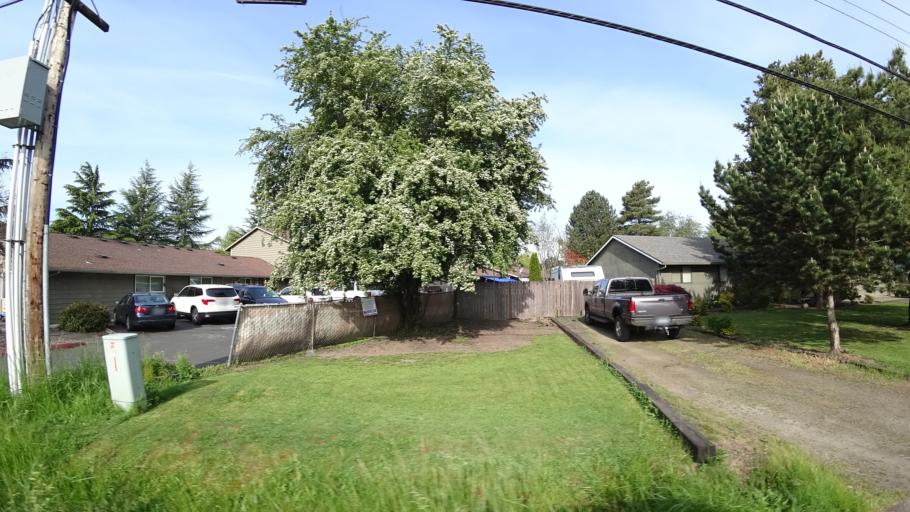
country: US
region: Oregon
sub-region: Washington County
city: Hillsboro
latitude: 45.5324
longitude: -122.9645
